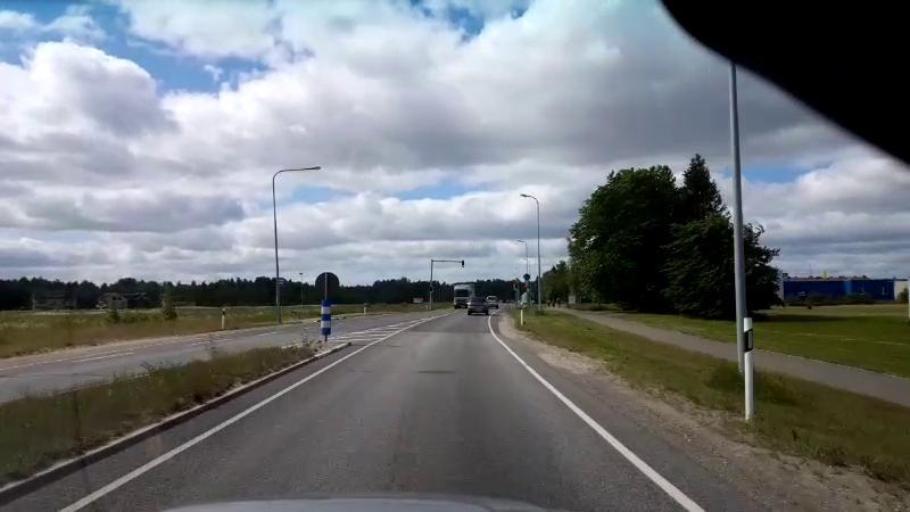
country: EE
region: Paernumaa
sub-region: Sauga vald
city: Sauga
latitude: 58.4281
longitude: 24.4979
